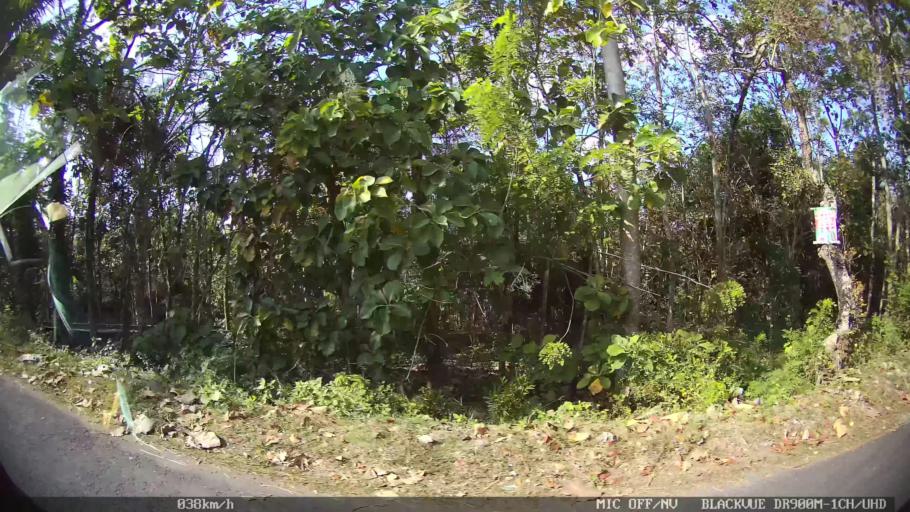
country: ID
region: Daerah Istimewa Yogyakarta
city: Kasihan
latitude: -7.8177
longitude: 110.2957
